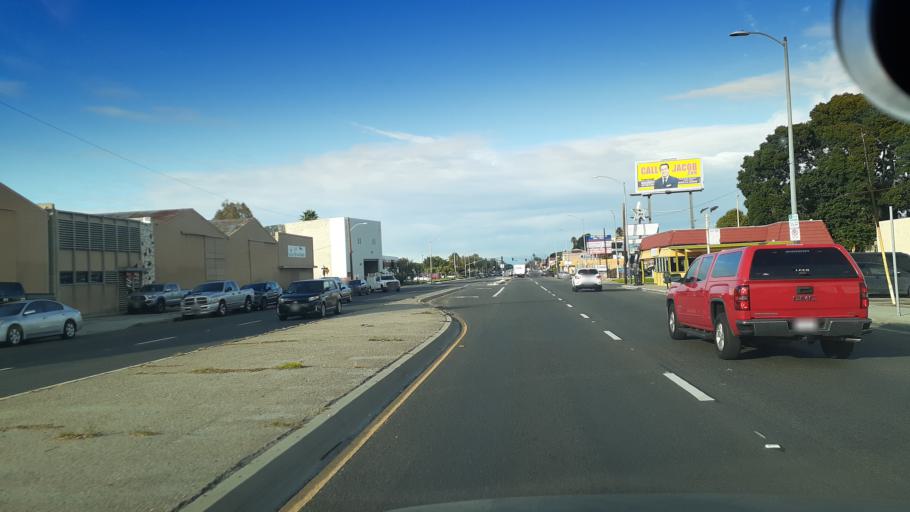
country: US
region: California
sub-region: Los Angeles County
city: West Carson
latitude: 33.8219
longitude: -118.3089
